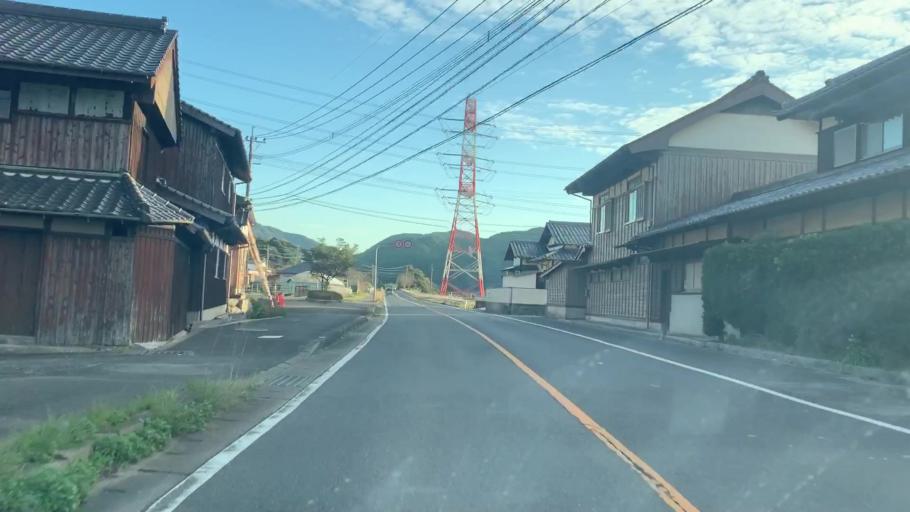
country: JP
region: Saga Prefecture
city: Karatsu
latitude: 33.3882
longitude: 129.9877
